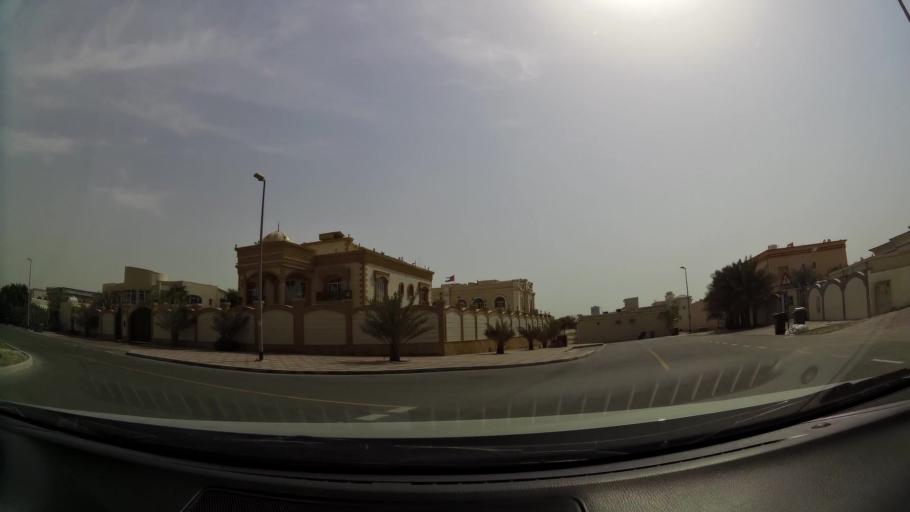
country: AE
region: Ash Shariqah
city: Sharjah
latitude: 25.2554
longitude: 55.4353
